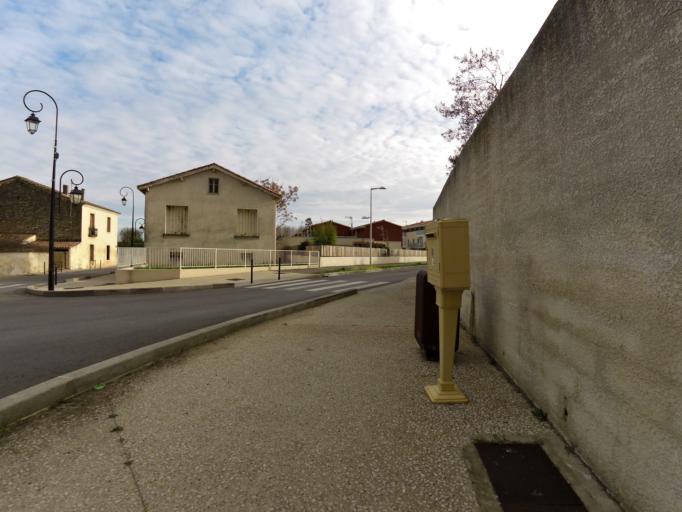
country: FR
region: Languedoc-Roussillon
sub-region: Departement de l'Herault
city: Castries
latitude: 43.6760
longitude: 3.9892
